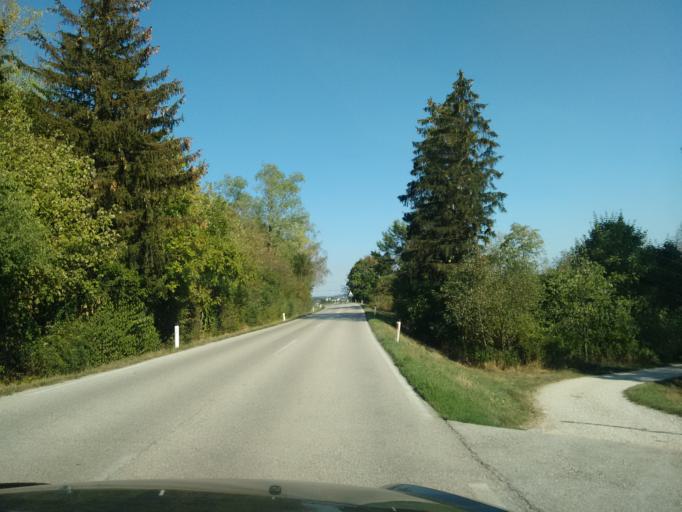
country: AT
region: Upper Austria
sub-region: Politischer Bezirk Linz-Land
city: Horsching
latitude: 48.2222
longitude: 14.2055
